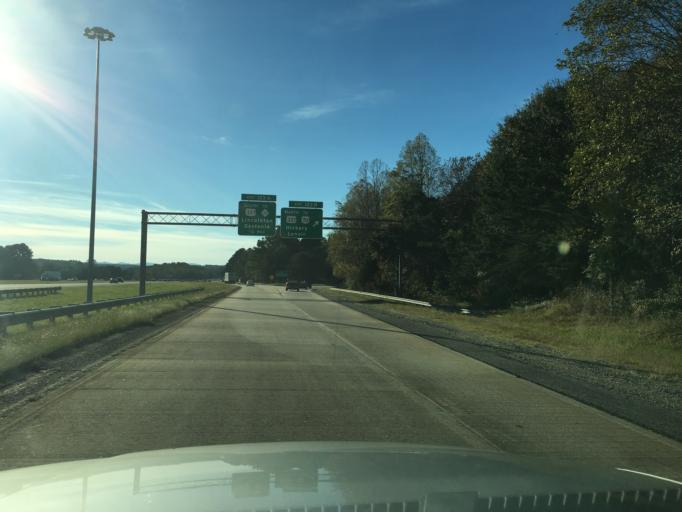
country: US
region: North Carolina
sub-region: Catawba County
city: Hickory
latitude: 35.7095
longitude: -81.3476
